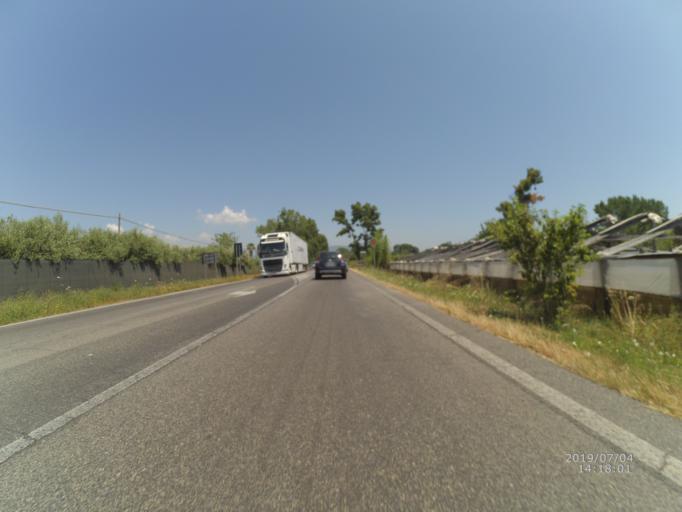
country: IT
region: Latium
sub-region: Provincia di Latina
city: Monte San Biagio
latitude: 41.2892
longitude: 13.3697
